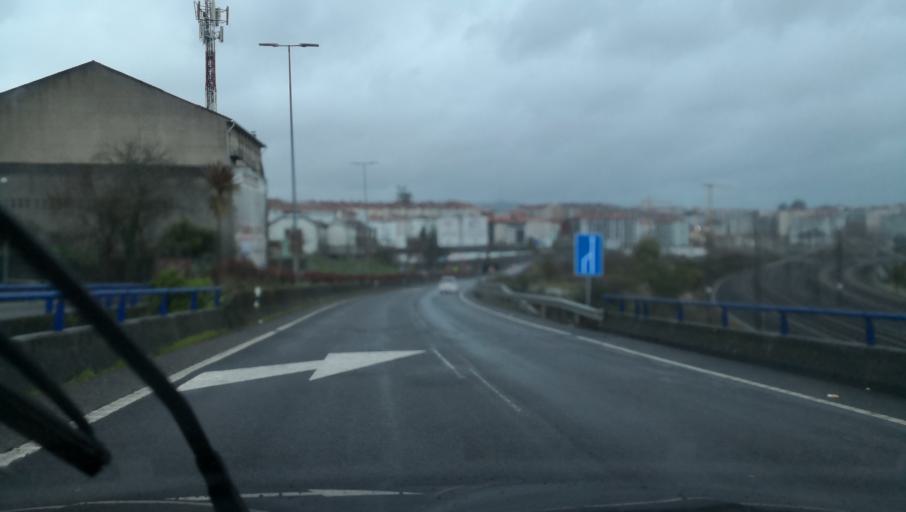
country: ES
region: Galicia
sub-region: Provincia da Coruna
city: Santiago de Compostela
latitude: 42.8652
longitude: -8.5523
